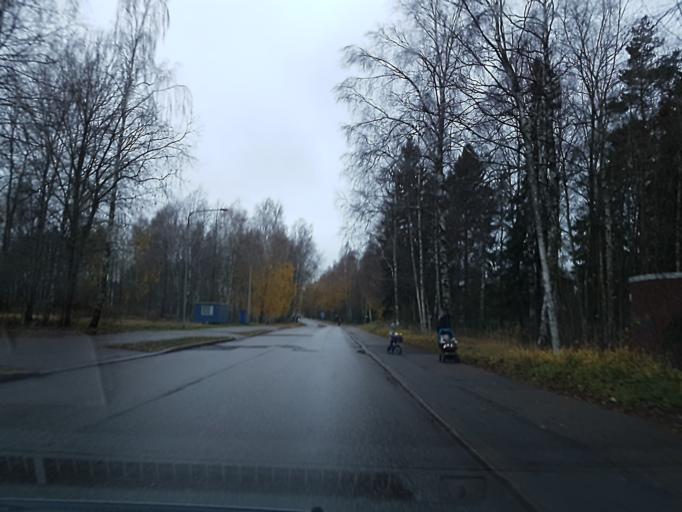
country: FI
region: Uusimaa
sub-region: Helsinki
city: Vantaa
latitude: 60.2300
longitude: 25.0884
